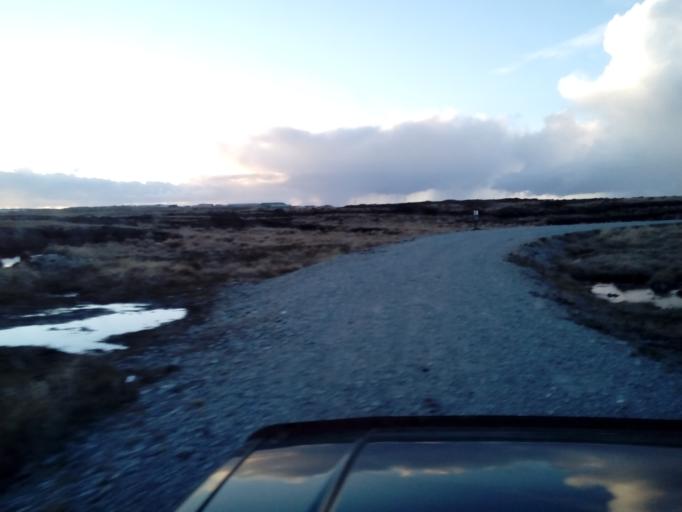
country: FK
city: Stanley
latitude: -51.7042
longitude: -57.8440
